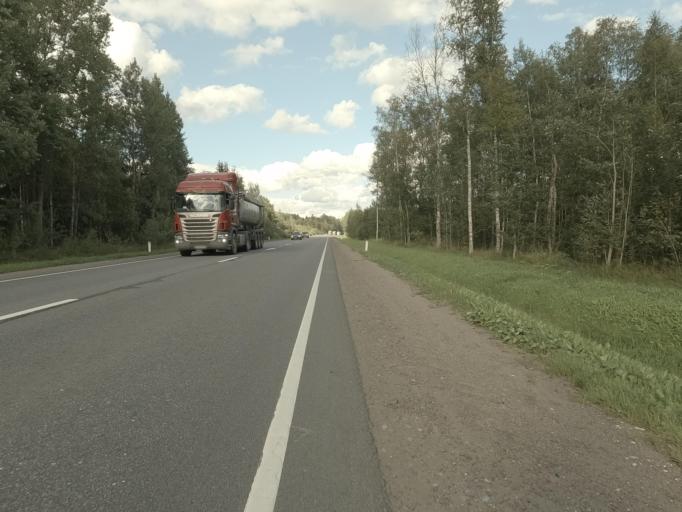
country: RU
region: Leningrad
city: Nikol'skoye
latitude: 59.6634
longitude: 30.8779
